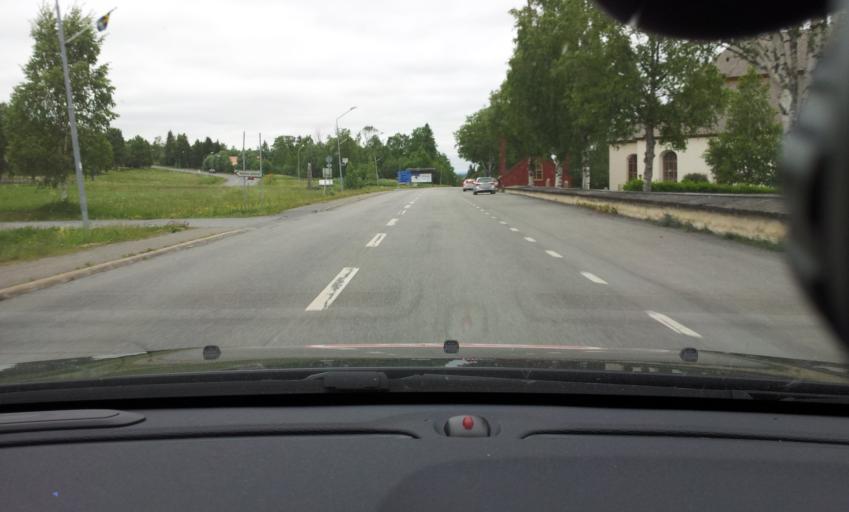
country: SE
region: Jaemtland
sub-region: Krokoms Kommun
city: Krokom
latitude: 63.1774
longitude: 14.0912
